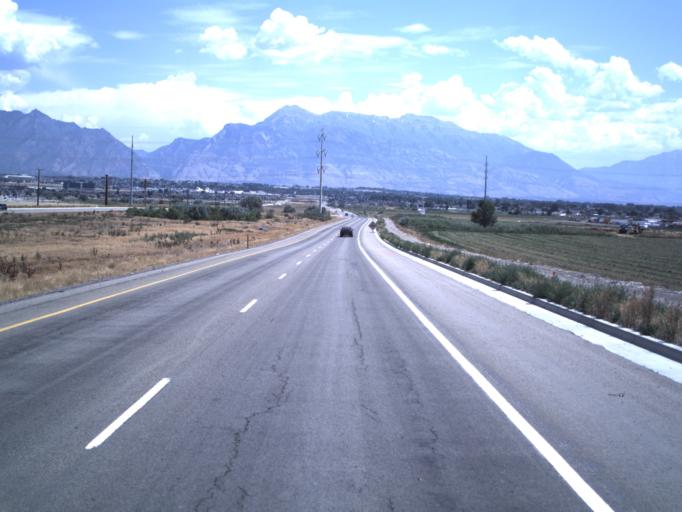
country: US
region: Utah
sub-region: Utah County
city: Saratoga Springs
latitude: 40.4126
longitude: -111.9153
